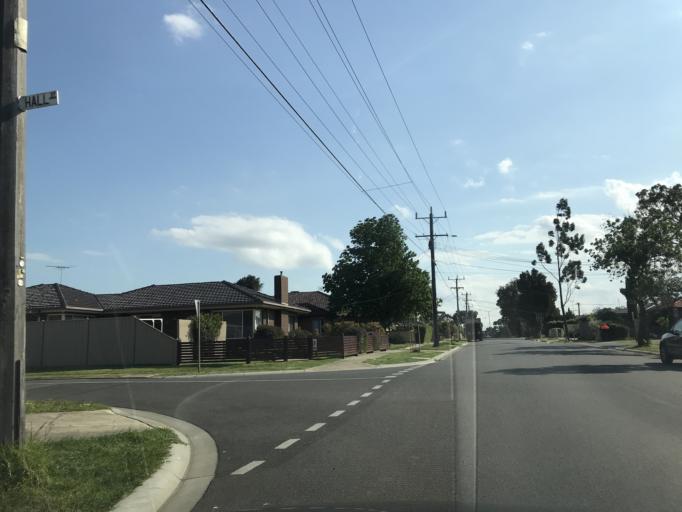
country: AU
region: Victoria
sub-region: Wyndham
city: Hoppers Crossing
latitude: -37.8762
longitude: 144.6978
